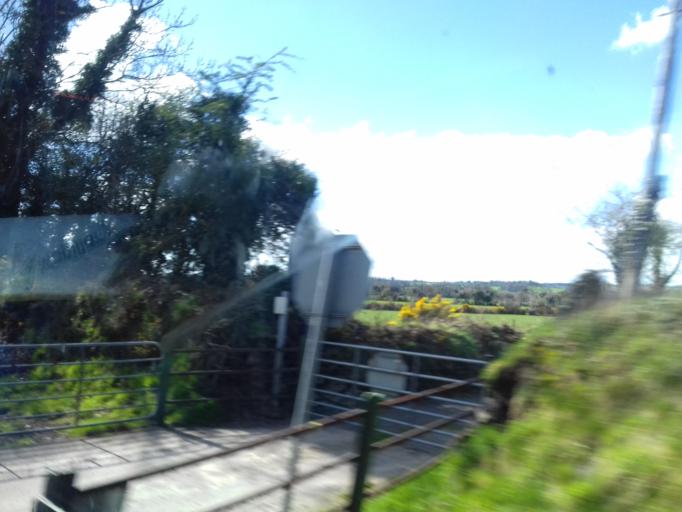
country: IE
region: Munster
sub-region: County Cork
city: Kanturk
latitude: 52.1239
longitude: -8.9145
